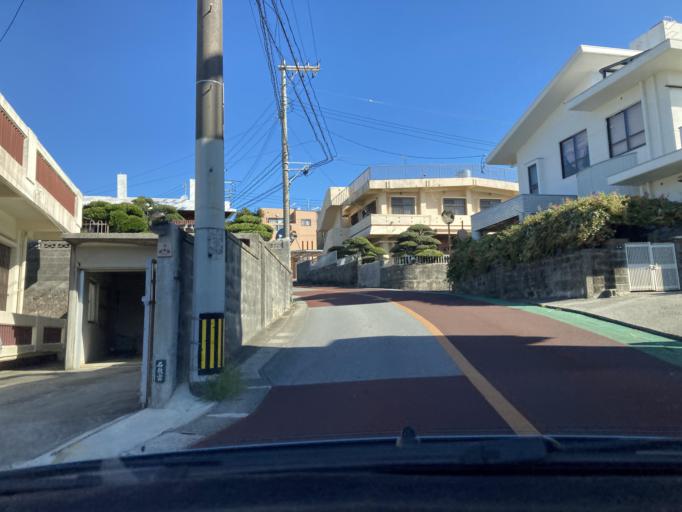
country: JP
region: Okinawa
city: Chatan
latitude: 26.3033
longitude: 127.7982
